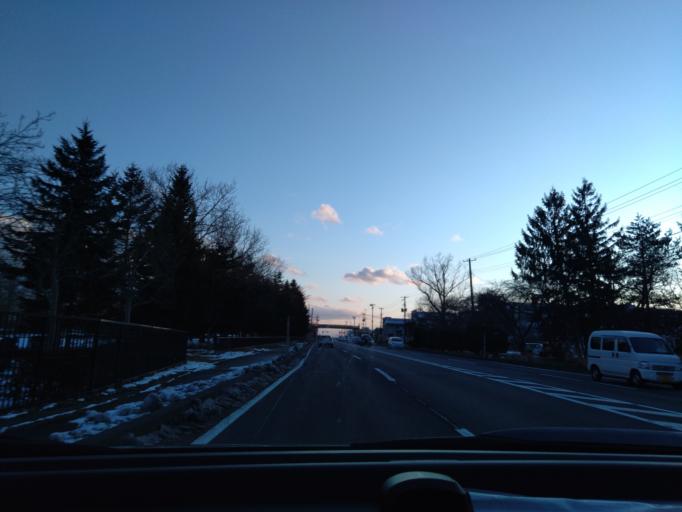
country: JP
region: Iwate
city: Hanamaki
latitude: 39.4244
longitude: 141.1298
